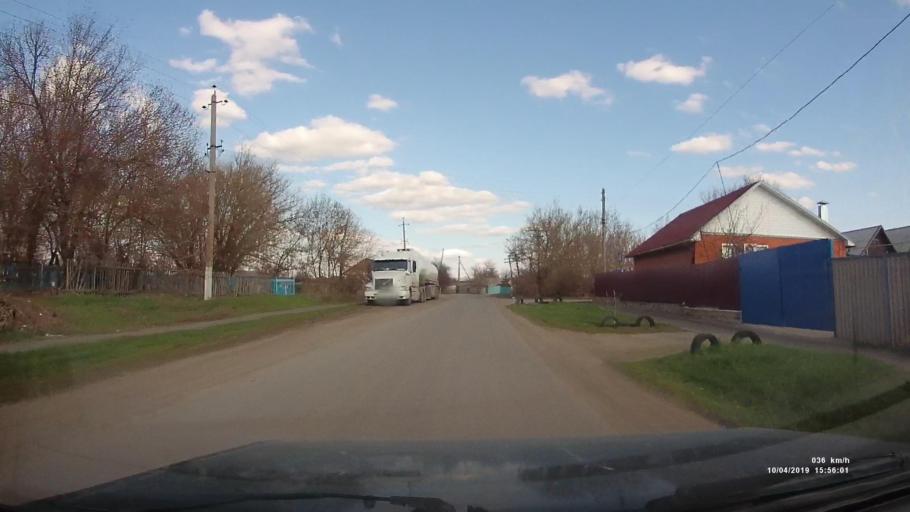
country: RU
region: Rostov
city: Masalovka
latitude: 48.4123
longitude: 40.2693
